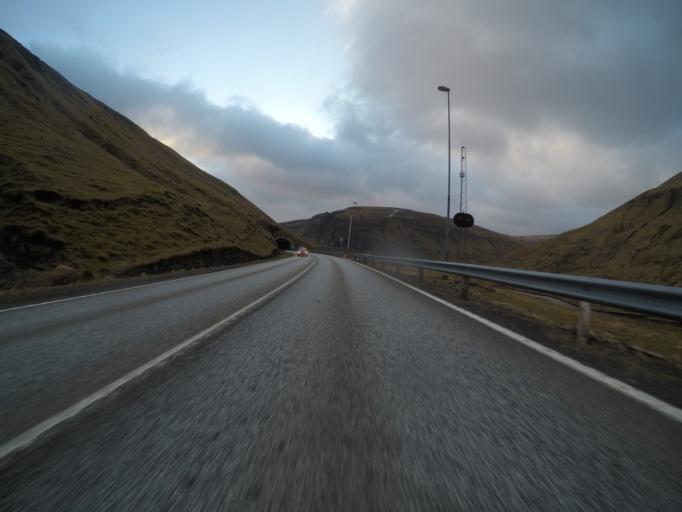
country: FO
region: Streymoy
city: Kollafjordhur
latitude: 62.1279
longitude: -7.0095
